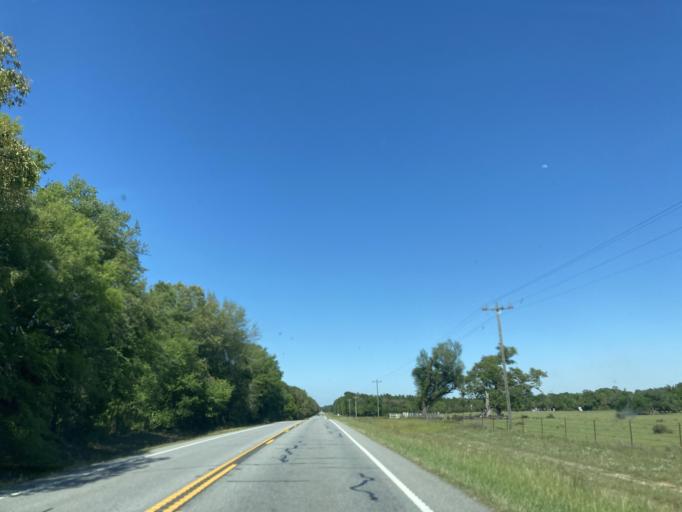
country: US
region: Georgia
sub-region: Baker County
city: Newton
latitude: 31.1921
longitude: -84.5156
